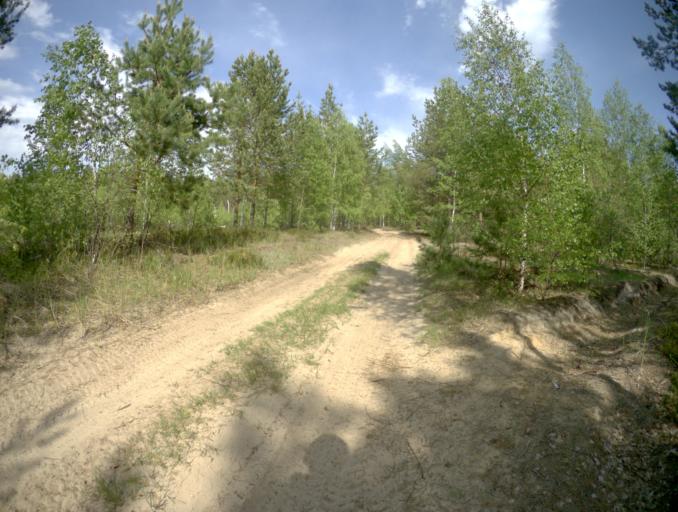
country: RU
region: Vladimir
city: Ivanishchi
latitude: 55.6859
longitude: 40.3735
